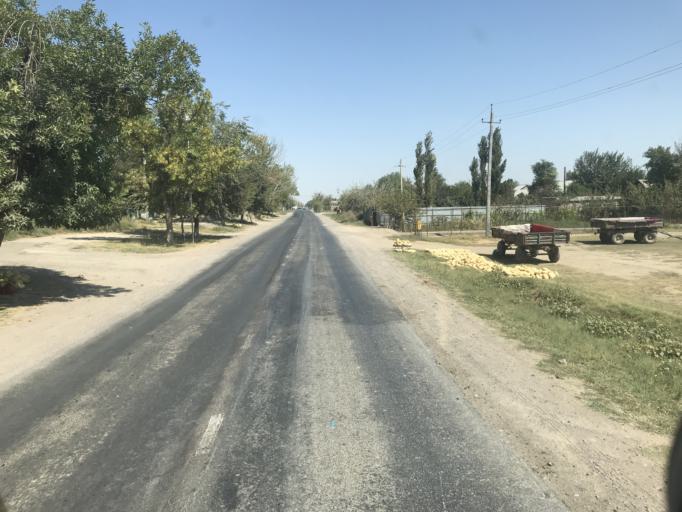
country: KZ
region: Ongtustik Qazaqstan
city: Ilyich
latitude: 40.9282
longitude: 68.4883
